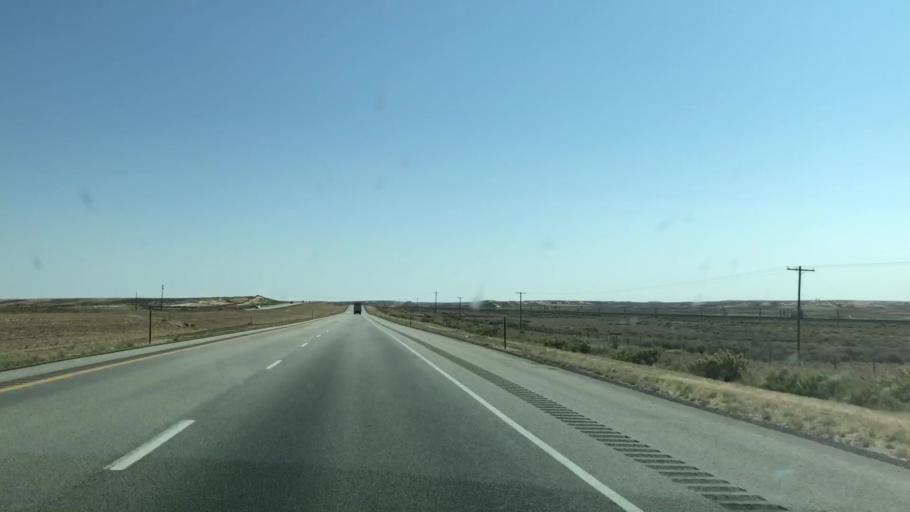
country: US
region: Wyoming
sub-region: Carbon County
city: Rawlins
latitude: 41.6952
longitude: -107.9268
